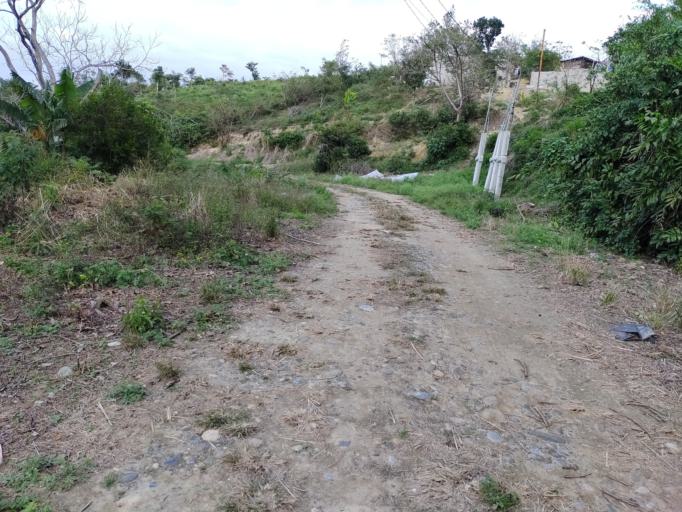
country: MX
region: Veracruz
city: Papantla de Olarte
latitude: 20.4486
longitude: -97.3086
